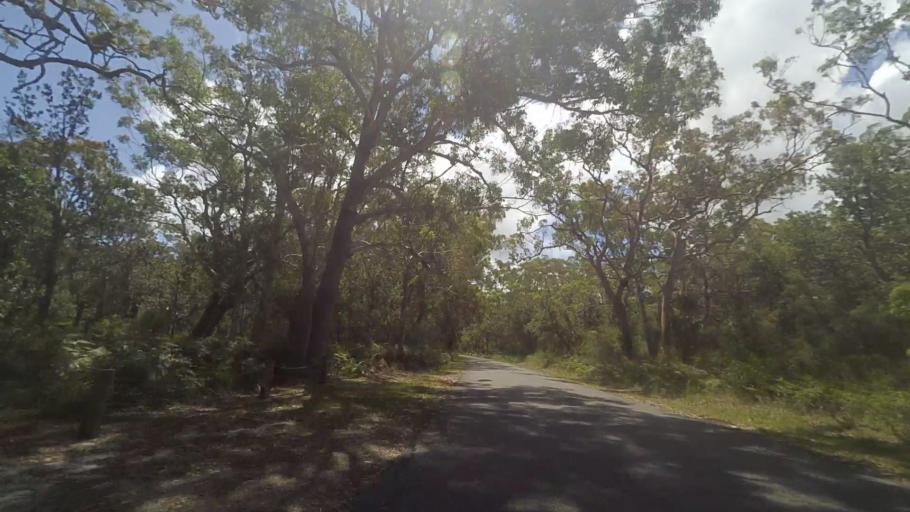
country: AU
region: New South Wales
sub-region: Great Lakes
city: Bulahdelah
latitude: -32.5049
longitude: 152.3128
